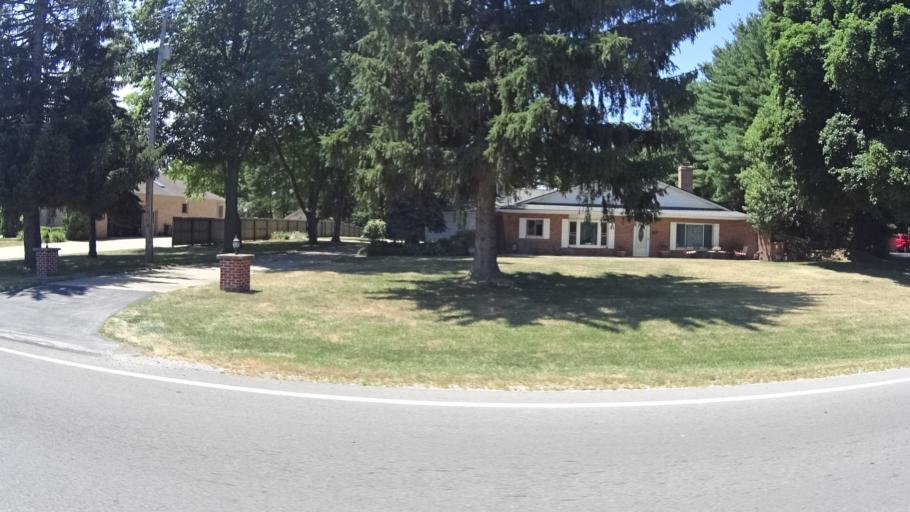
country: US
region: Ohio
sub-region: Erie County
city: Sandusky
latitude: 41.4216
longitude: -82.7033
